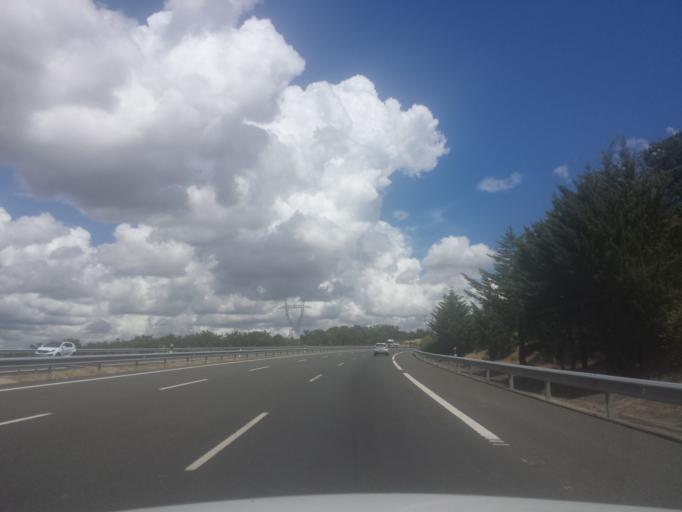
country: ES
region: Castille and Leon
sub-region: Provincia de Salamanca
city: Puerto de Bejar
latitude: 40.3621
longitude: -5.8363
